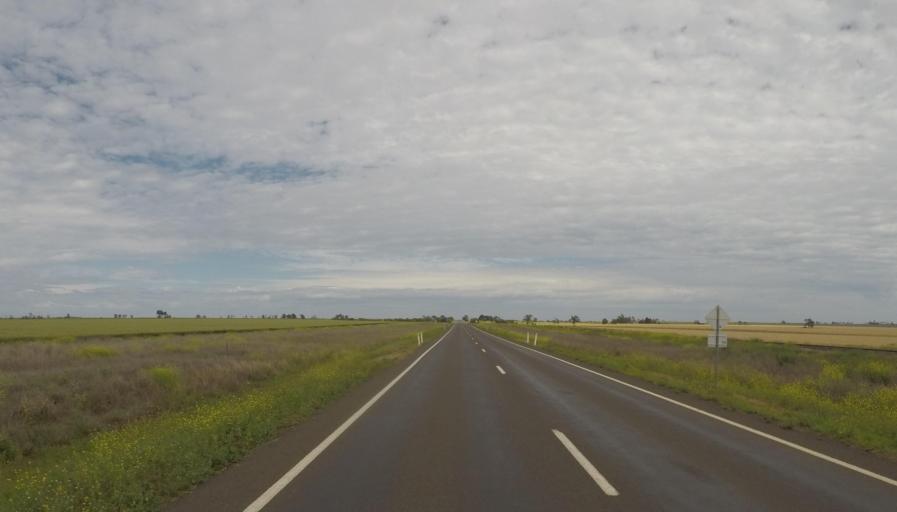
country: AU
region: Queensland
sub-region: Maranoa
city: Roma
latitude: -26.5898
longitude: 148.4709
